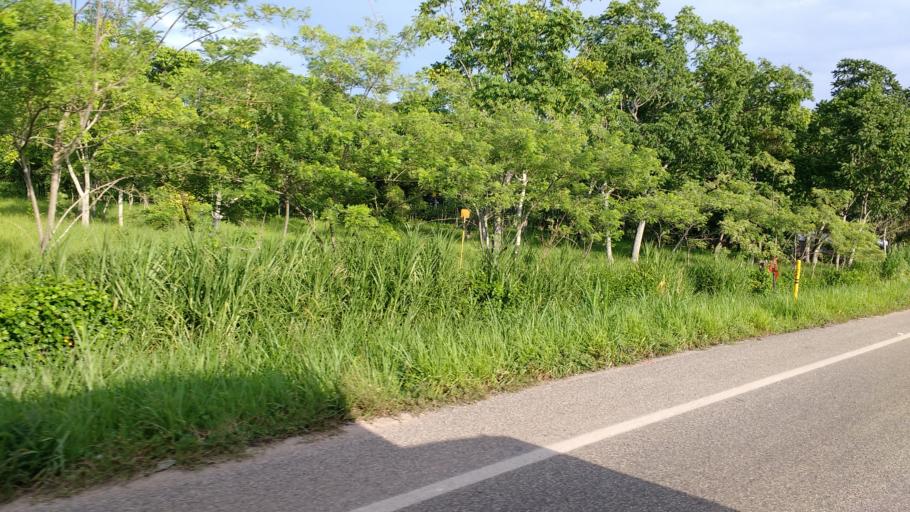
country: MX
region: Tabasco
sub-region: Teapa
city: Eureka y Belen
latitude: 17.6255
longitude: -92.9627
